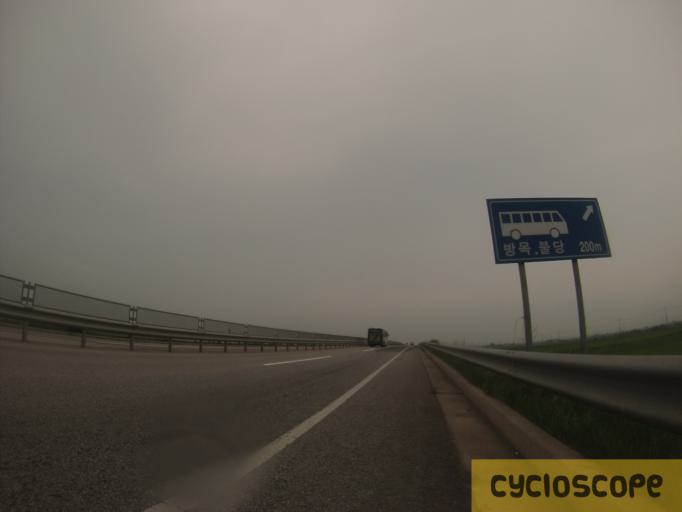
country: KR
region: Jeollabuk-do
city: Kimje
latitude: 35.8545
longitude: 126.8166
